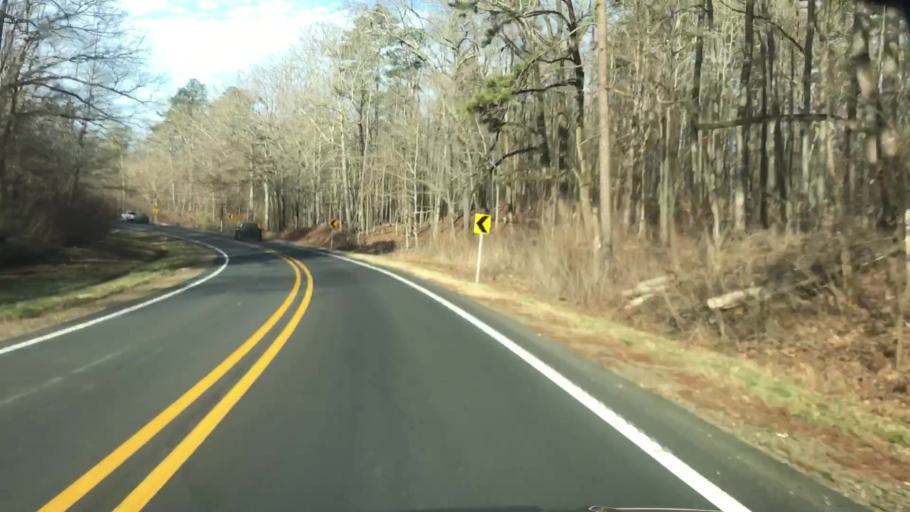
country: US
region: Arkansas
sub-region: Montgomery County
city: Mount Ida
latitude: 34.5232
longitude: -93.3925
